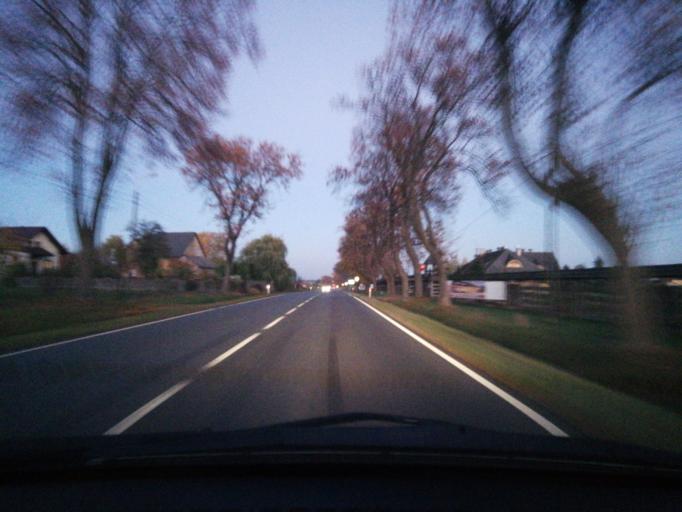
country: PL
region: Lodz Voivodeship
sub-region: Powiat brzezinski
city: Rogow
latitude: 51.8099
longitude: 19.9252
